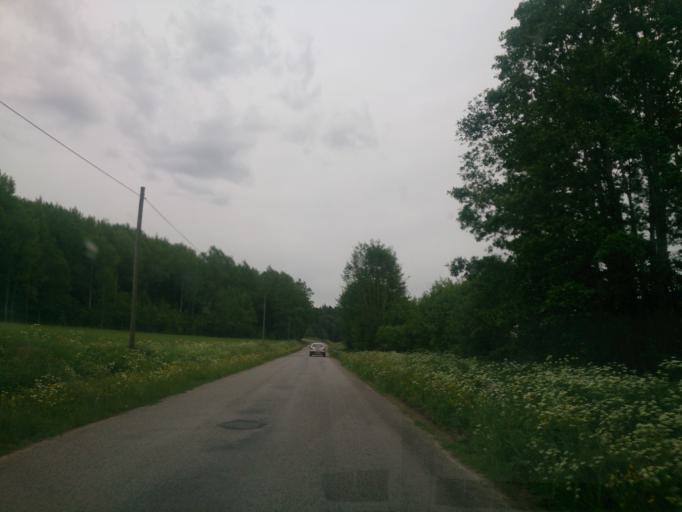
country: SE
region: OEstergoetland
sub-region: Soderkopings Kommun
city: Soederkoeping
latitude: 58.3168
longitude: 16.3092
